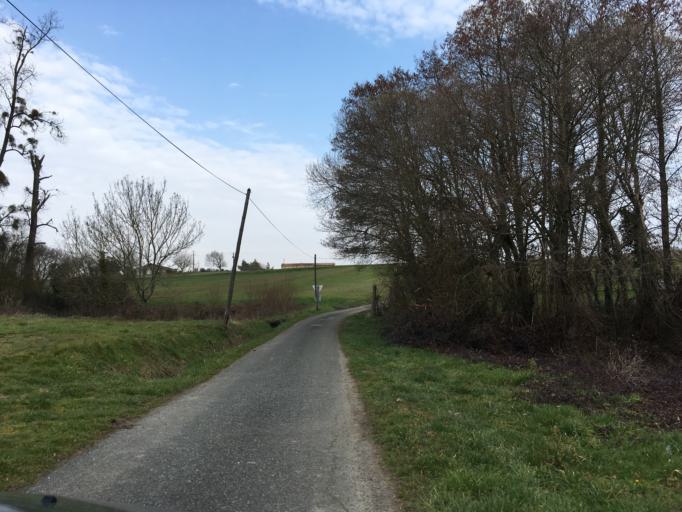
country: FR
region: Poitou-Charentes
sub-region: Departement de la Charente-Maritime
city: Mirambeau
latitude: 45.3311
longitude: -0.5875
